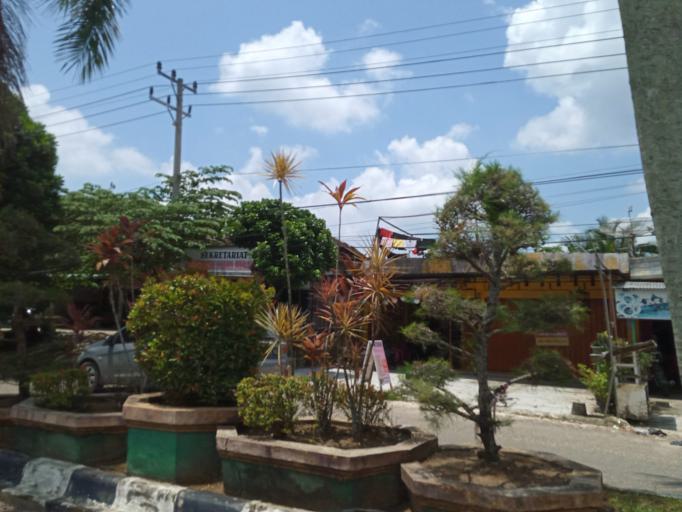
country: ID
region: Jambi
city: Bangko
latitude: -2.0539
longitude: 102.2819
